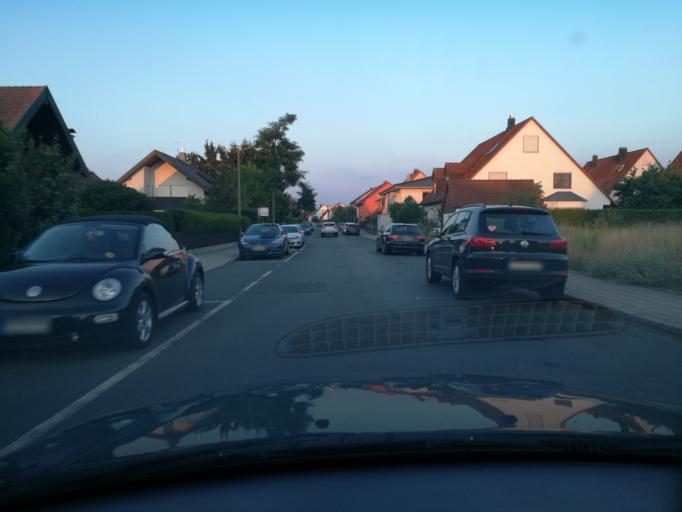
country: DE
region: Bavaria
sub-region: Regierungsbezirk Mittelfranken
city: Seukendorf
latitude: 49.4919
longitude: 10.9106
